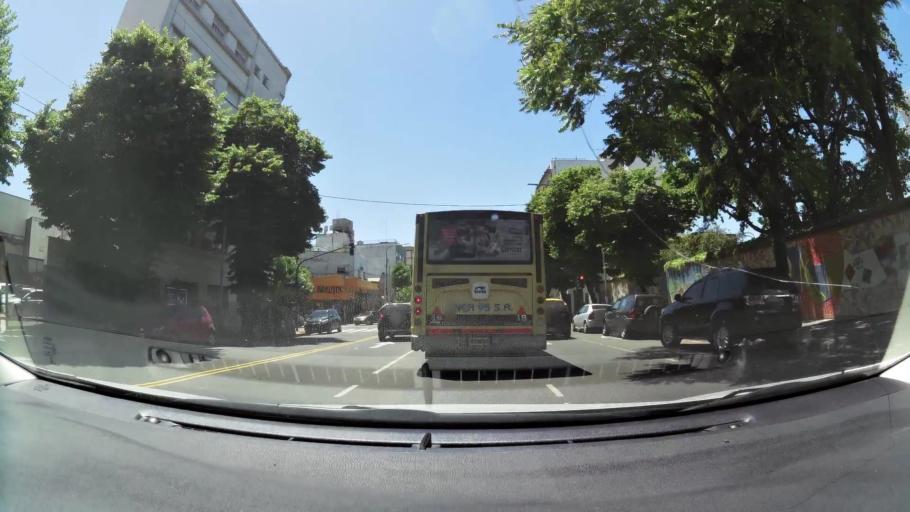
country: AR
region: Buenos Aires F.D.
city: Buenos Aires
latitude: -34.6335
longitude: -58.3880
